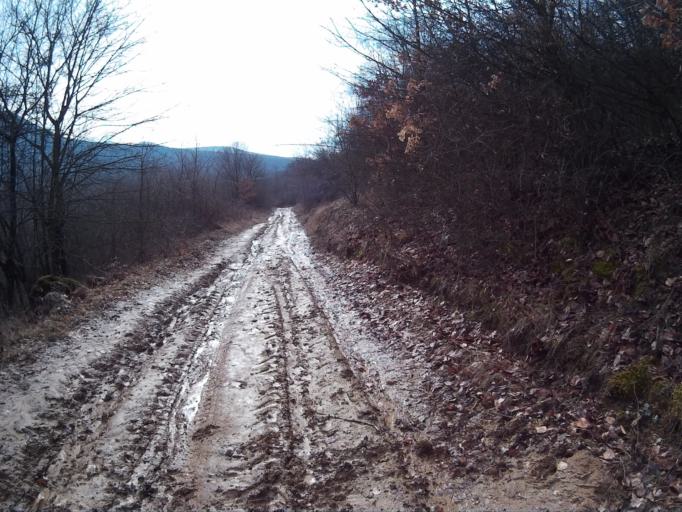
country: HU
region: Borsod-Abauj-Zemplen
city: Satoraljaujhely
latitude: 48.4068
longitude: 21.6000
